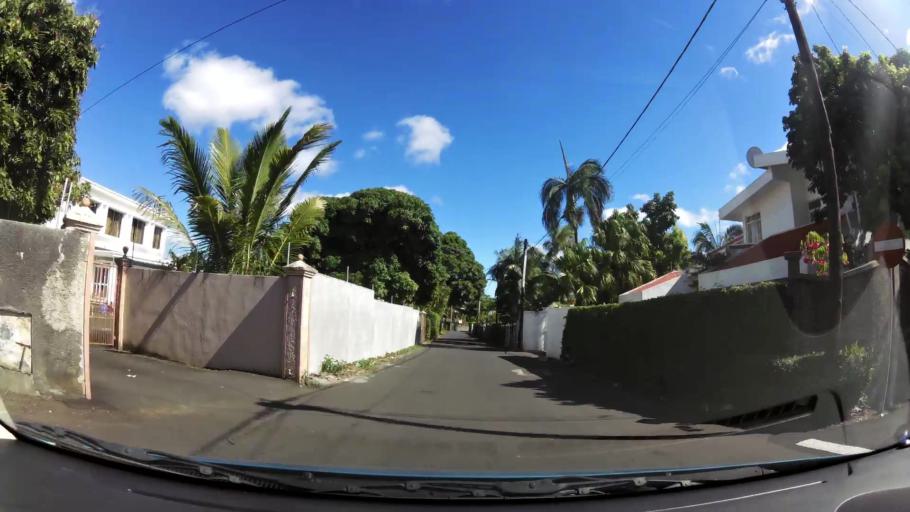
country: MU
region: Plaines Wilhems
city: Vacoas
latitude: -20.2993
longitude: 57.4879
